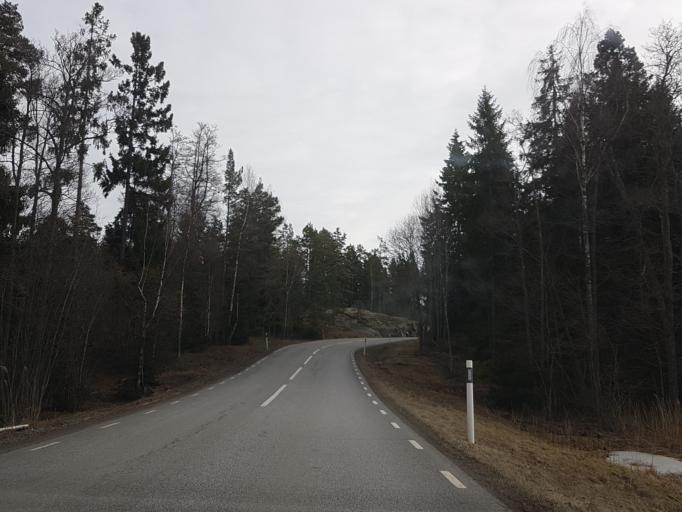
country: SE
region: Stockholm
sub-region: Norrtalje Kommun
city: Norrtalje
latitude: 59.6741
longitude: 18.8399
